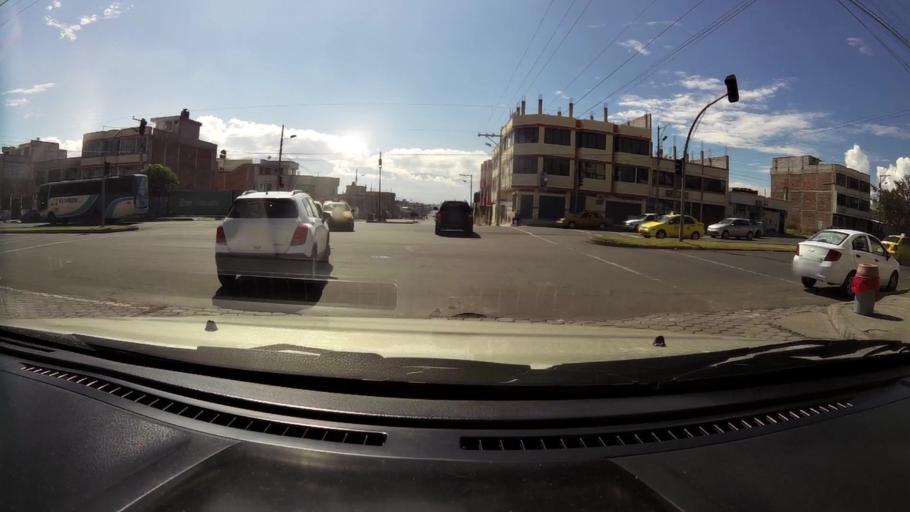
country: EC
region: Chimborazo
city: Riobamba
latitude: -1.6582
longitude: -78.6727
